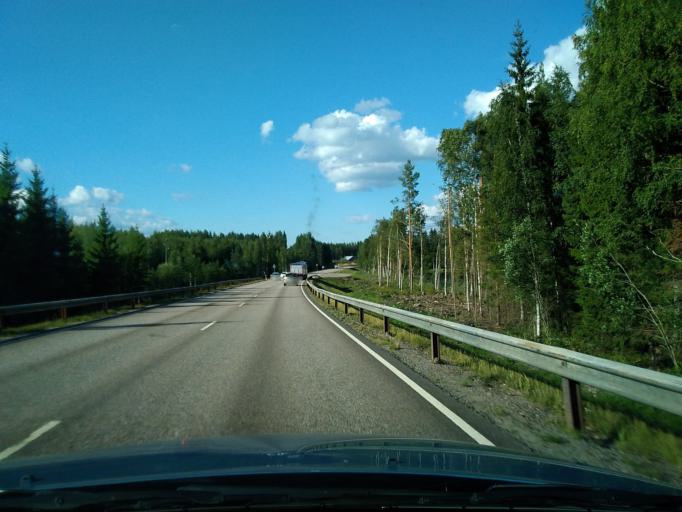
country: FI
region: Pirkanmaa
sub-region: Ylae-Pirkanmaa
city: Maenttae
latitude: 62.0925
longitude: 24.7278
